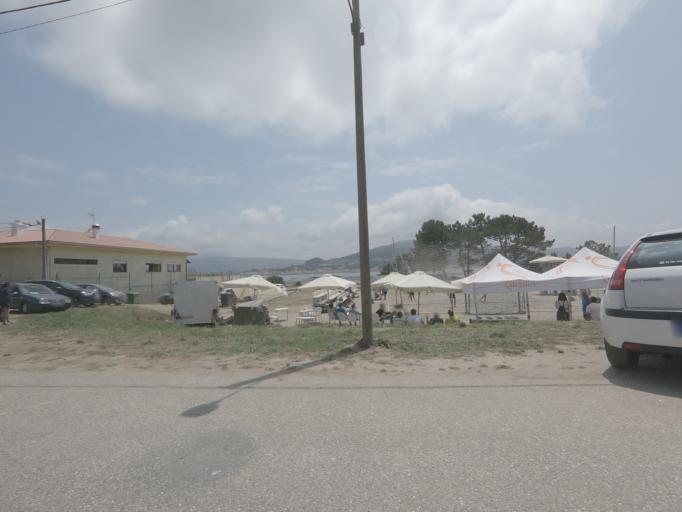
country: ES
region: Galicia
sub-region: Provincia de Pontevedra
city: A Guarda
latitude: 41.8851
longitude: -8.8561
